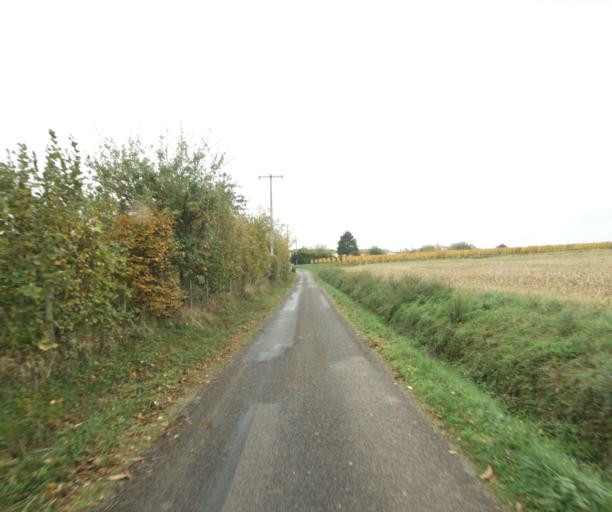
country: FR
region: Bourgogne
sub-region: Departement de Saone-et-Loire
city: Saint-Martin-Belle-Roche
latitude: 46.4701
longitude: 4.8537
